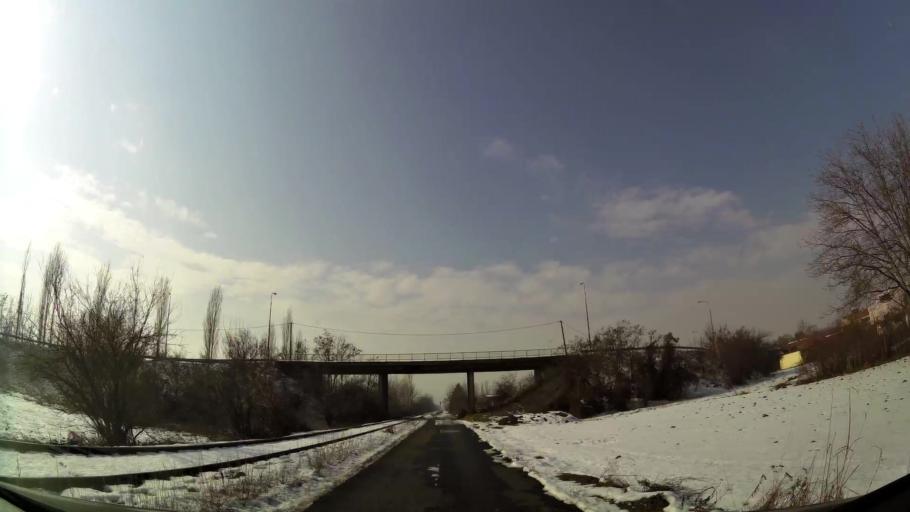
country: MK
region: Suto Orizari
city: Suto Orizare
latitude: 42.0246
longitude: 21.3850
